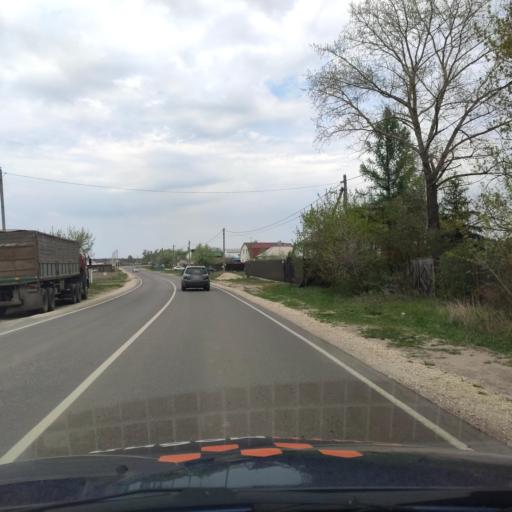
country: RU
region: Voronezj
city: Podgornoye
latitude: 51.8511
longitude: 39.1495
